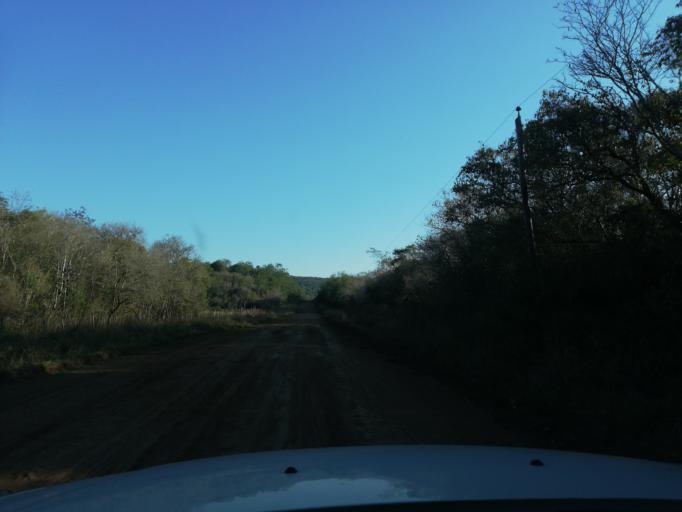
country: AR
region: Misiones
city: Cerro Cora
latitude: -27.6003
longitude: -55.6990
